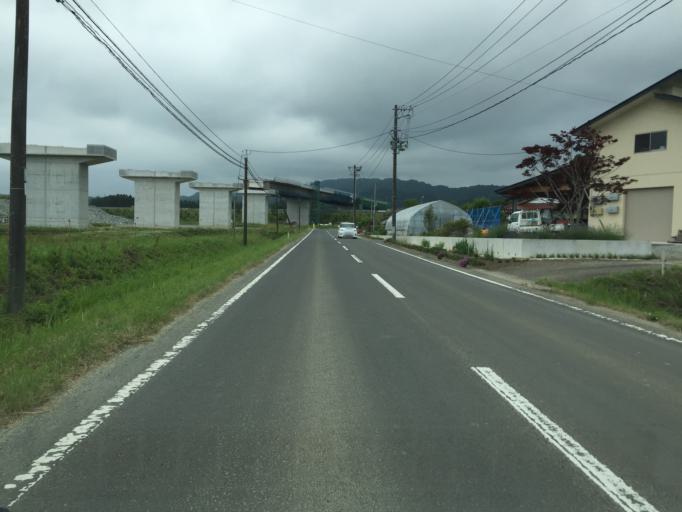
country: JP
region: Miyagi
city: Marumori
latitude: 37.7777
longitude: 140.9007
